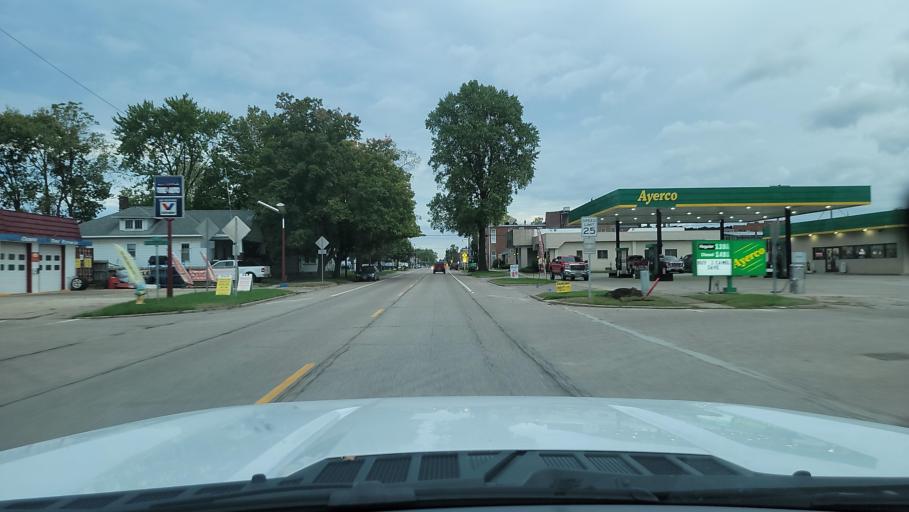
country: US
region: Illinois
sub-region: Schuyler County
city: Rushville
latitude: 40.1189
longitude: -90.5636
